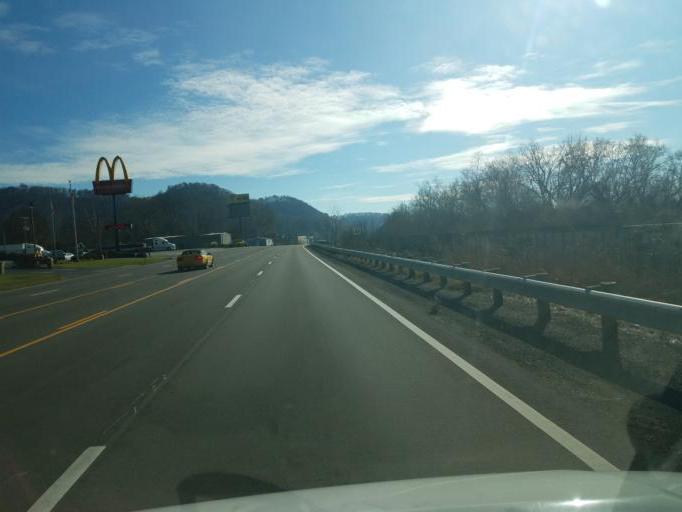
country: US
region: Ohio
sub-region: Scioto County
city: Rosemount
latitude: 38.7890
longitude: -82.9851
